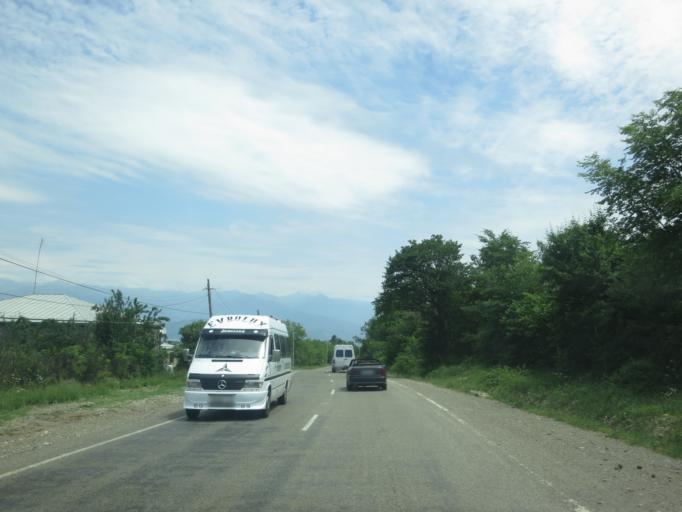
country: GE
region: Kakheti
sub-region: Telavi
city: Telavi
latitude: 41.9266
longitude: 45.4143
